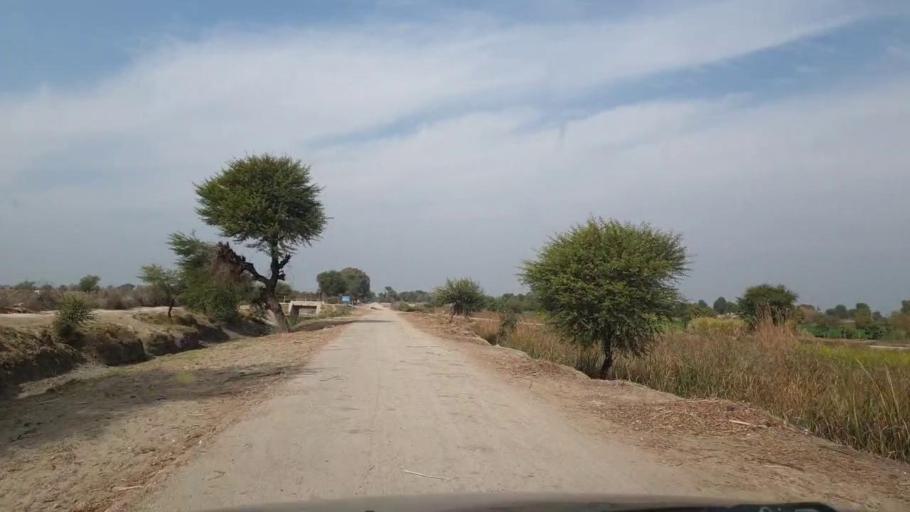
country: PK
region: Sindh
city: Khadro
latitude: 26.1207
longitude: 68.8023
